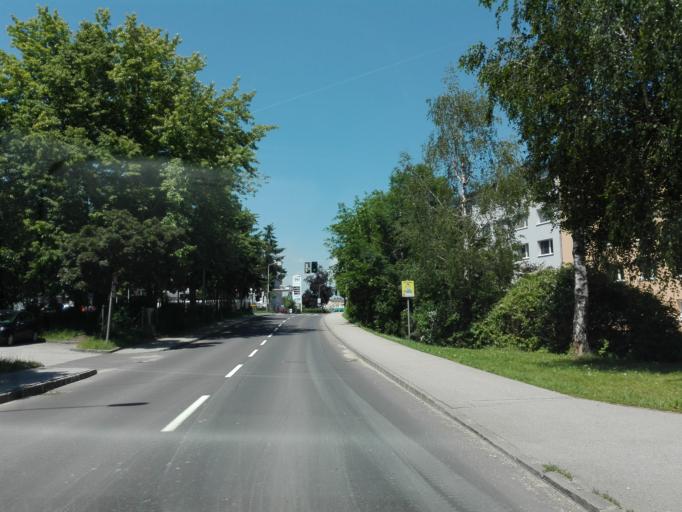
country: AT
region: Upper Austria
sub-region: Politischer Bezirk Linz-Land
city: Traun
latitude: 48.2021
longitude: 14.2503
